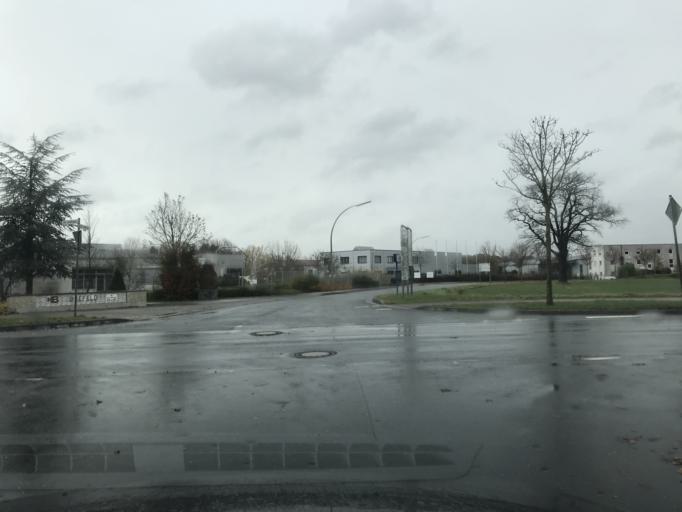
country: DE
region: North Rhine-Westphalia
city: Oelde
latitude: 51.8455
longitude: 8.1547
